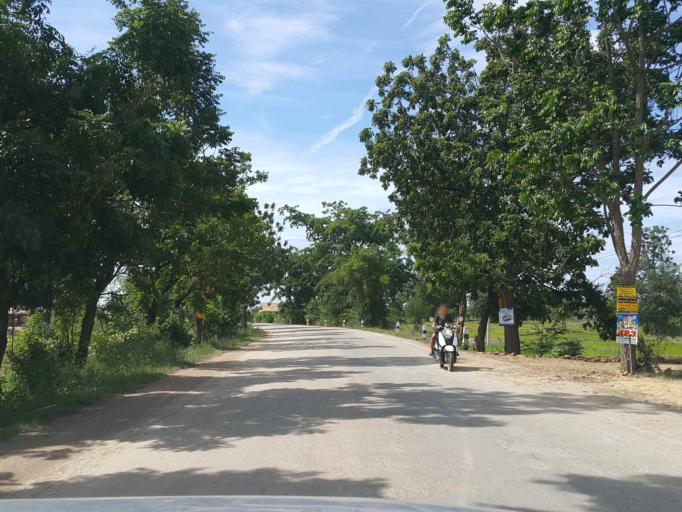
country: TH
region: Sukhothai
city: Ban Dan Lan Hoi
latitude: 17.1485
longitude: 99.5218
